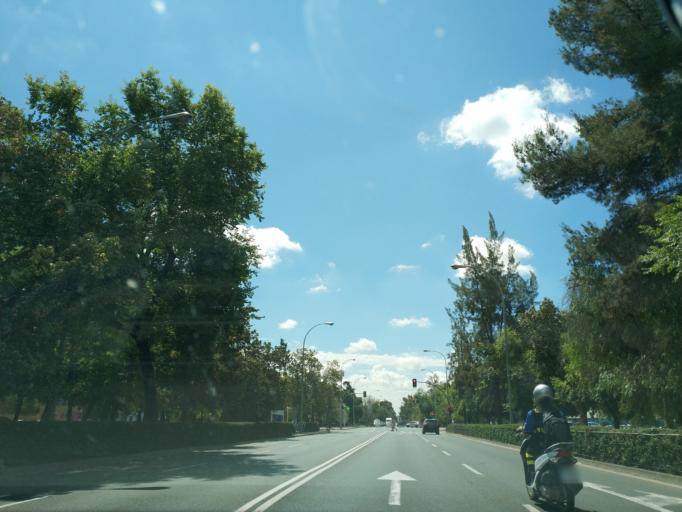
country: ES
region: Andalusia
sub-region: Provincia de Sevilla
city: Sevilla
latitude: 37.3677
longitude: -5.9672
